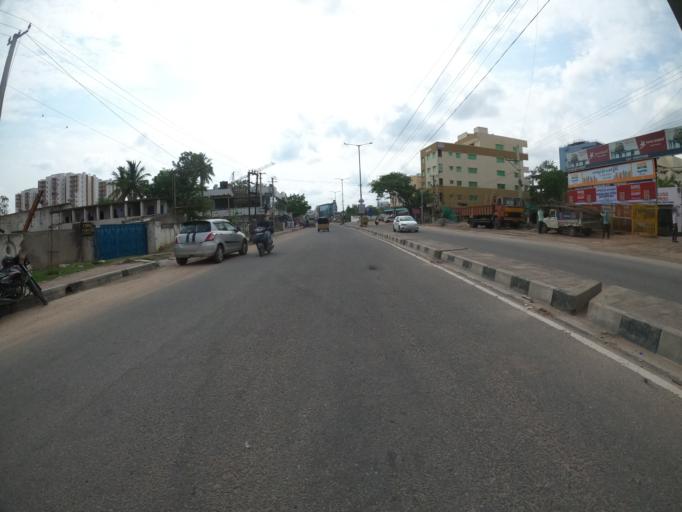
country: IN
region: Telangana
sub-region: Hyderabad
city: Hyderabad
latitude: 17.3834
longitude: 78.3632
